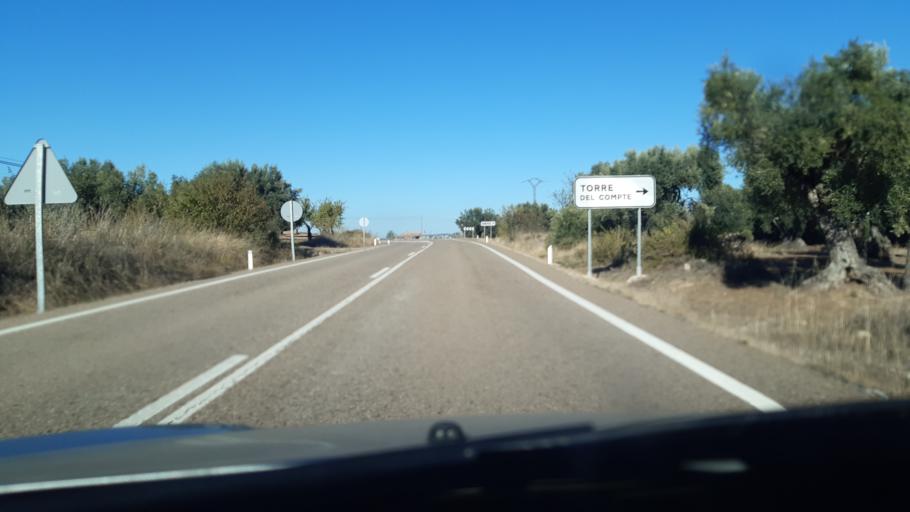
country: ES
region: Aragon
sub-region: Provincia de Teruel
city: Torre del Compte
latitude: 40.9268
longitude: 0.0816
